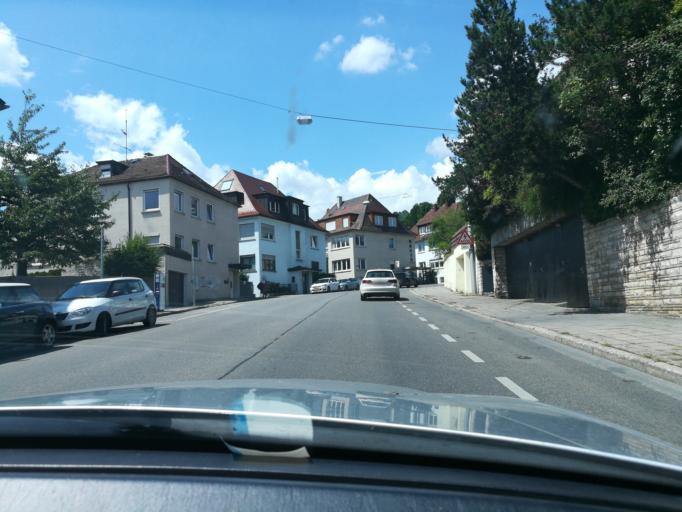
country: DE
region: Baden-Wuerttemberg
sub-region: Regierungsbezirk Stuttgart
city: Stuttgart
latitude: 48.7787
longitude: 9.1485
